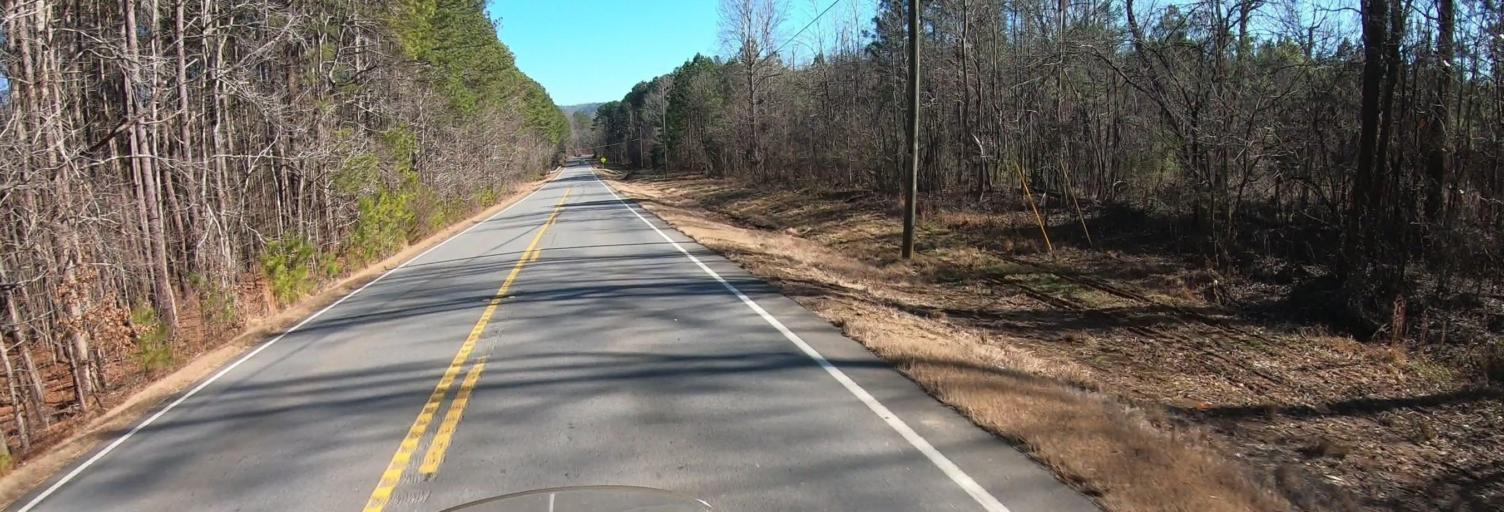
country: US
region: Georgia
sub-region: Murray County
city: Chatsworth
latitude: 34.5915
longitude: -84.6902
